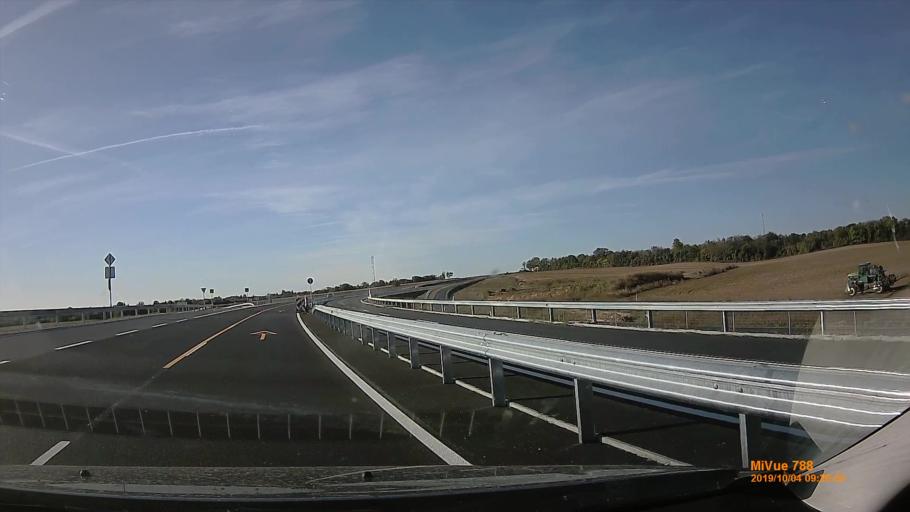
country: HU
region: Somogy
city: Kaposvar
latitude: 46.5211
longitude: 17.8182
